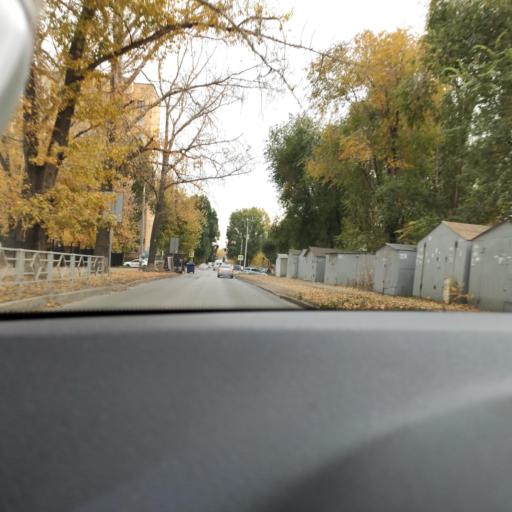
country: RU
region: Samara
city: Samara
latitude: 53.2385
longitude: 50.2513
